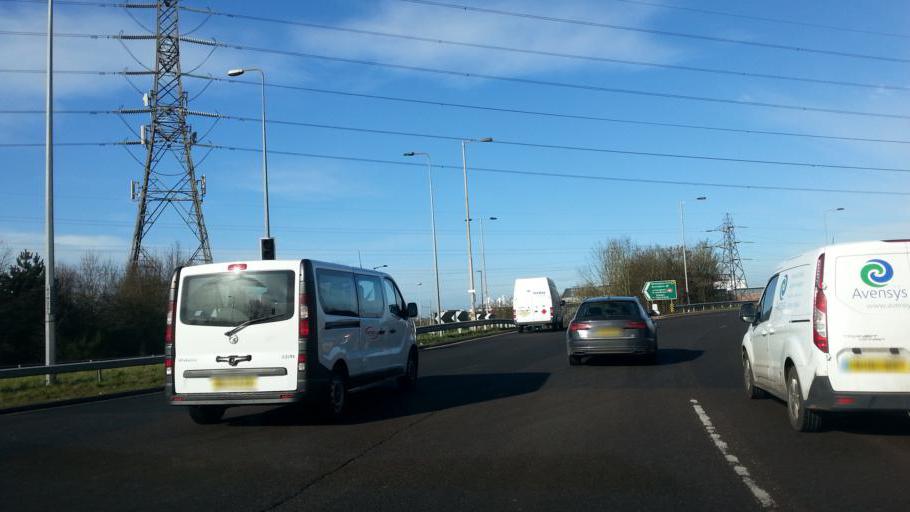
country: GB
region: England
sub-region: Solihull
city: Bickenhill
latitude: 52.4441
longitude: -1.7111
